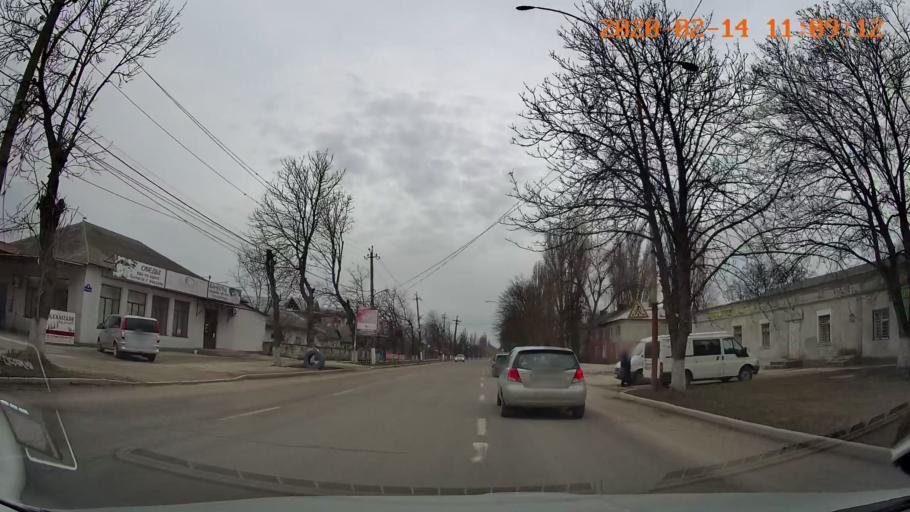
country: MD
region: Raionul Edinet
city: Edinet
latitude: 48.1766
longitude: 27.2959
